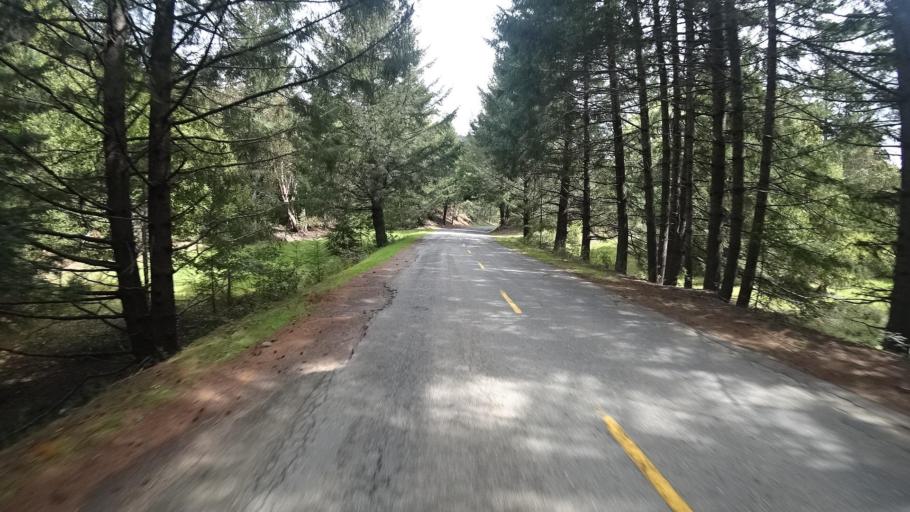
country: US
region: California
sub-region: Humboldt County
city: Redway
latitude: 40.1191
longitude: -123.6714
